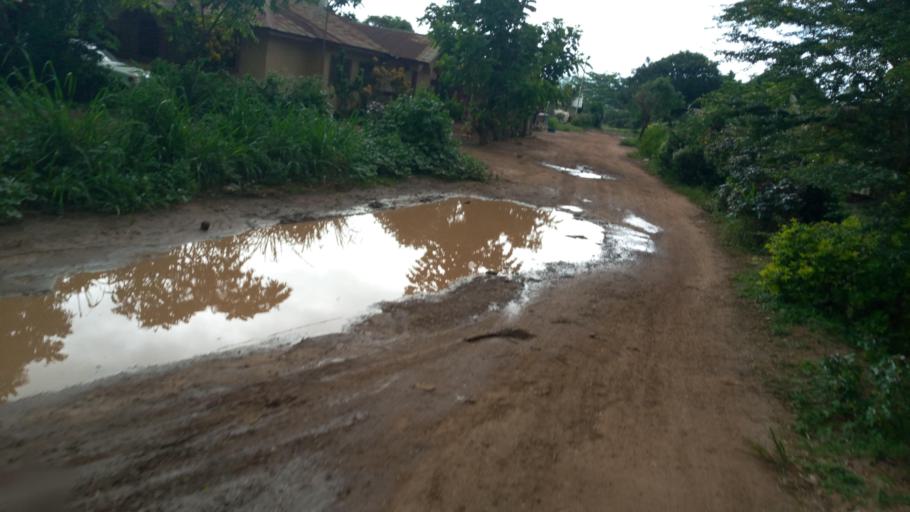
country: SL
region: Southern Province
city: Mogbwemo
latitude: 7.7809
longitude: -12.2914
